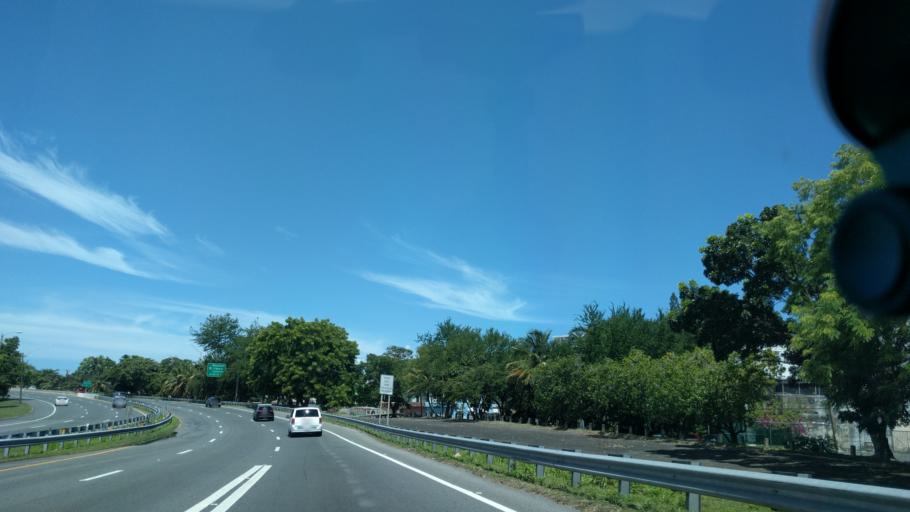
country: PR
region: San Juan
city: San Juan
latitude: 18.4390
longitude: -66.0628
